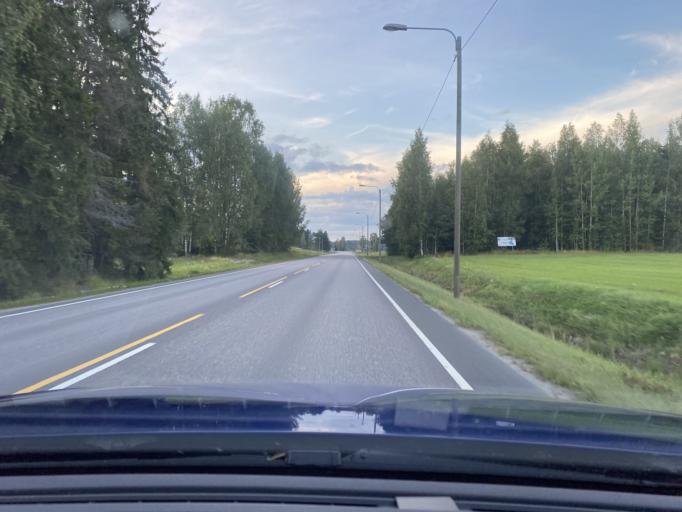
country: FI
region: Satakunta
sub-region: Pohjois-Satakunta
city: Kankaanpaeae
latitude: 61.7392
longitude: 22.5252
